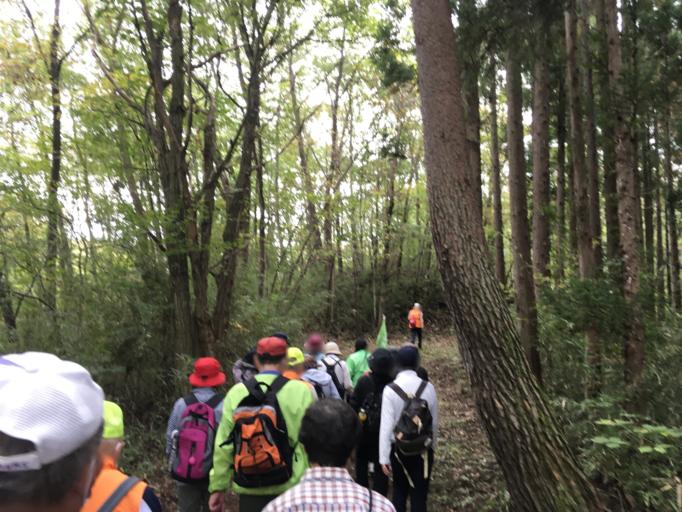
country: JP
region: Iwate
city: Ichinoseki
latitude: 38.8890
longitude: 141.0877
